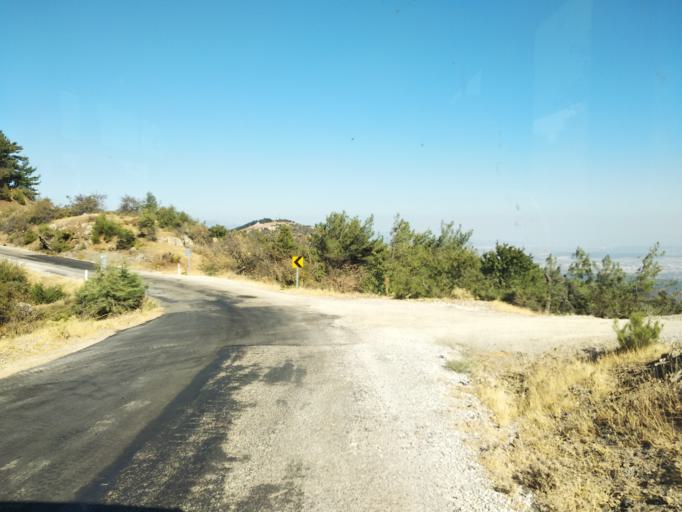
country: TR
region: Izmir
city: Gaziemir
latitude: 38.3127
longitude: 27.0026
